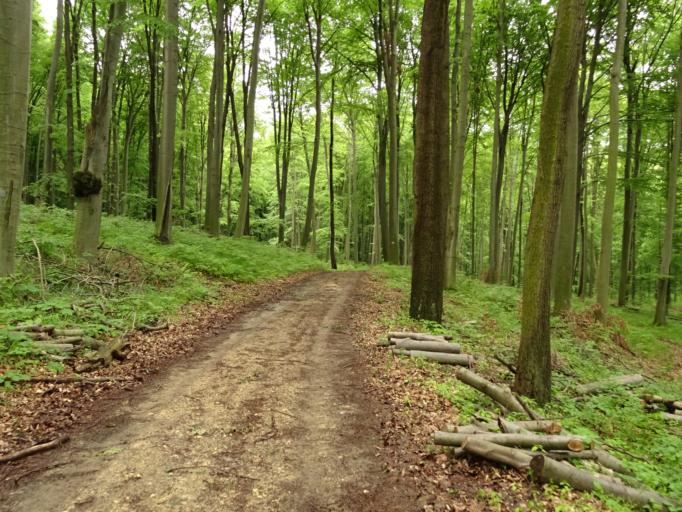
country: HU
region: Veszprem
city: Herend
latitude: 47.2179
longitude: 17.6609
